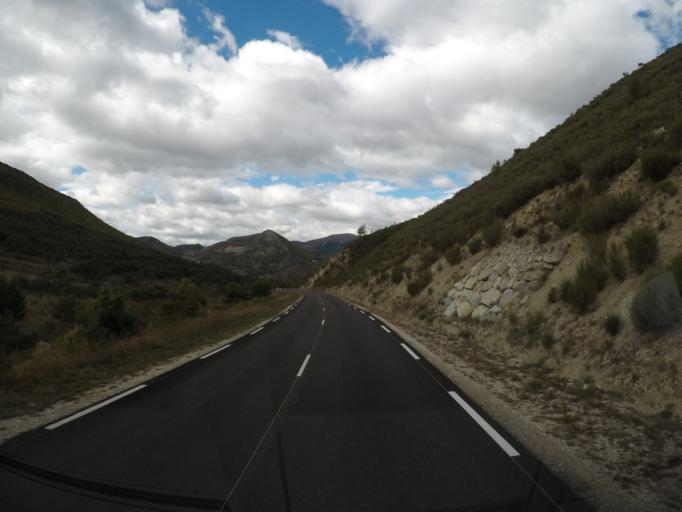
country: FR
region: Provence-Alpes-Cote d'Azur
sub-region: Departement du Vaucluse
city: Sault
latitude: 44.1836
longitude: 5.5574
